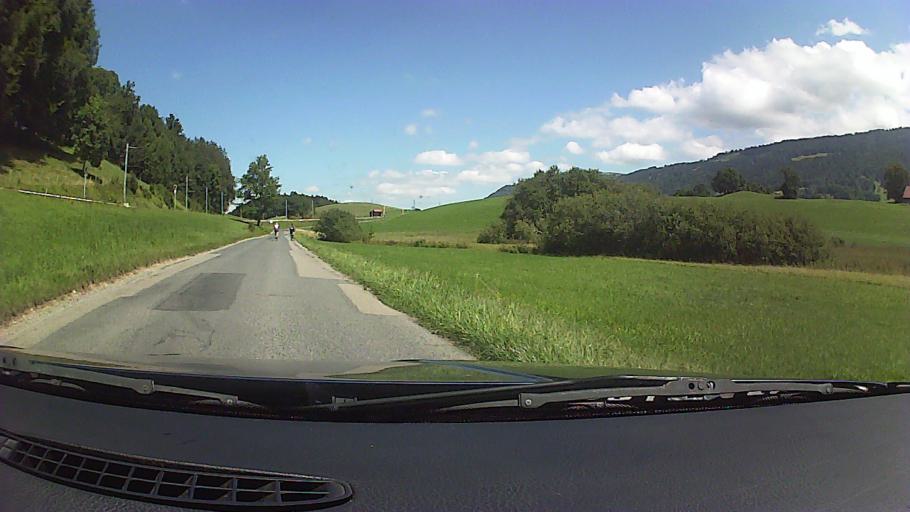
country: CH
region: Fribourg
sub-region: Veveyse District
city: Chatel-Saint-Denis
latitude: 46.5473
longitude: 6.8991
